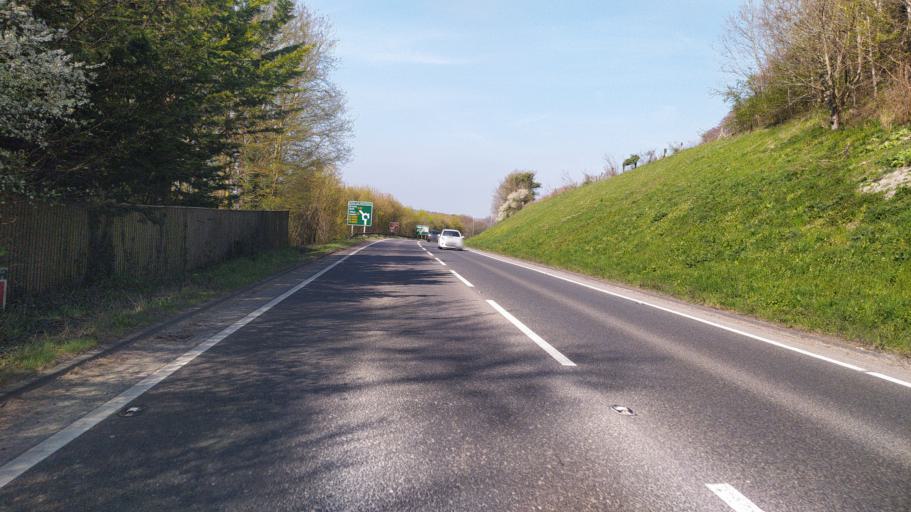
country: GB
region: England
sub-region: Wiltshire
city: Bishopstrow
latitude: 51.1848
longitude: -2.1153
